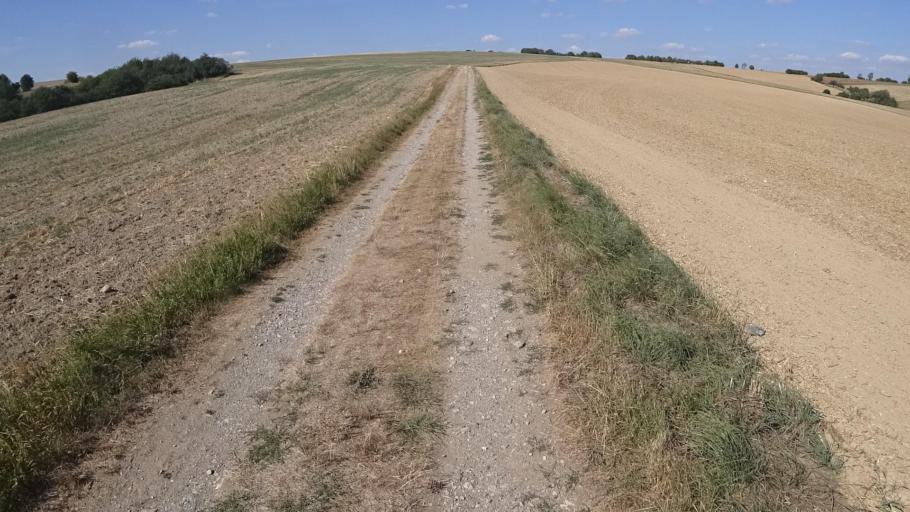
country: DE
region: Rheinland-Pfalz
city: Mengerschied
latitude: 49.9176
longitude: 7.5067
